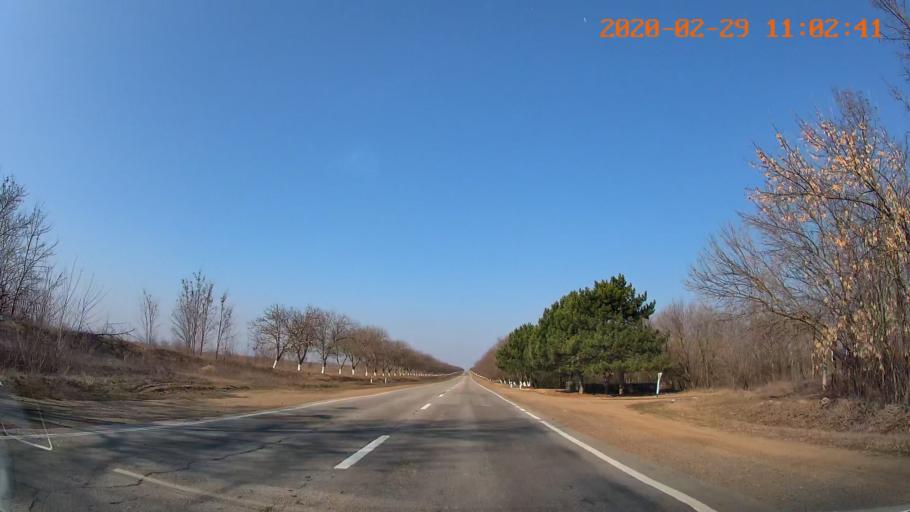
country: MD
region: Telenesti
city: Grigoriopol
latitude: 47.1743
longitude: 29.2330
